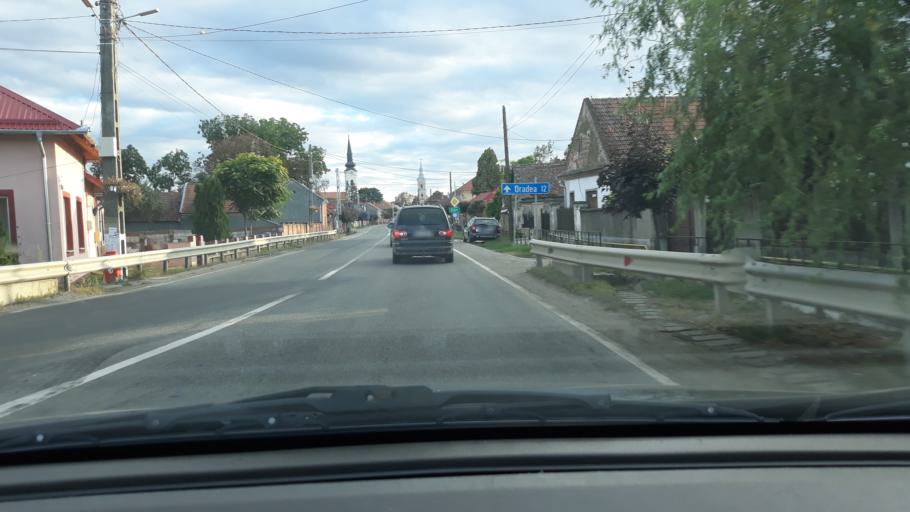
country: RO
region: Bihor
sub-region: Comuna Biharea
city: Biharea
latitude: 47.1568
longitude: 21.9220
